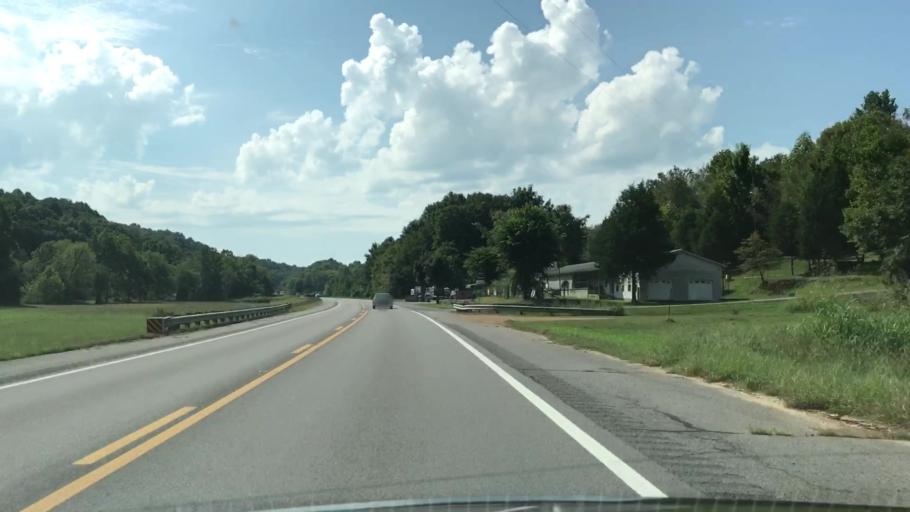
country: US
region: Tennessee
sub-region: Sumner County
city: Westmoreland
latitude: 36.6357
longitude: -86.2427
